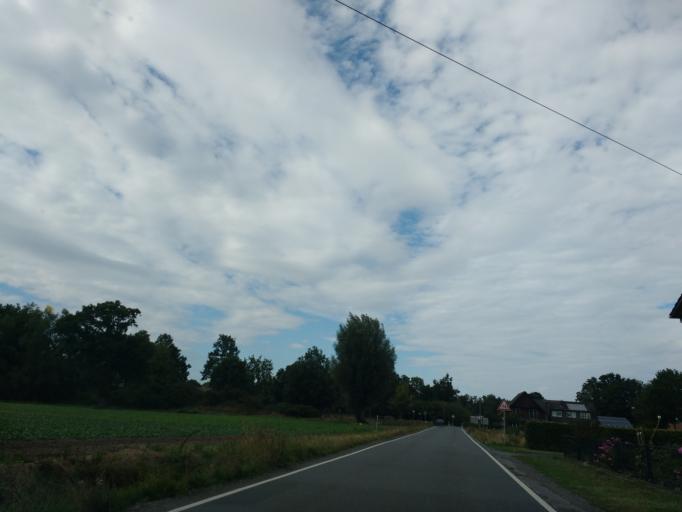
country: DE
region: North Rhine-Westphalia
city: Rietberg
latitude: 51.8147
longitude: 8.4490
